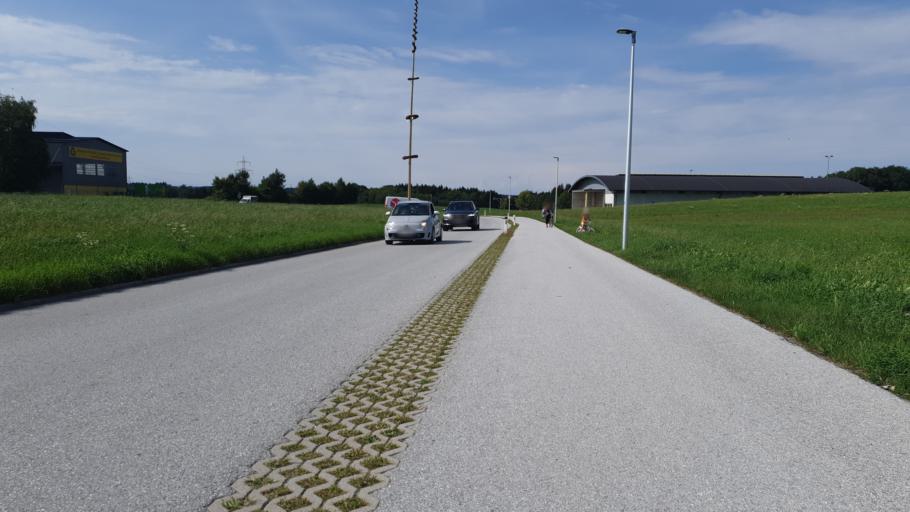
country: AT
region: Salzburg
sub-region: Politischer Bezirk Salzburg-Umgebung
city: Eugendorf
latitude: 47.8697
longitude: 13.1287
